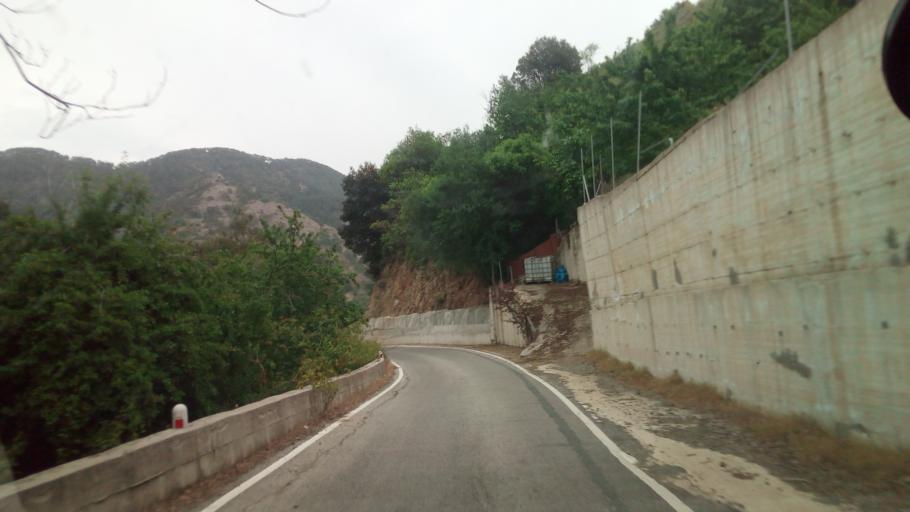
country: CY
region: Lefkosia
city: Kakopetria
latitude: 34.9633
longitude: 32.7460
